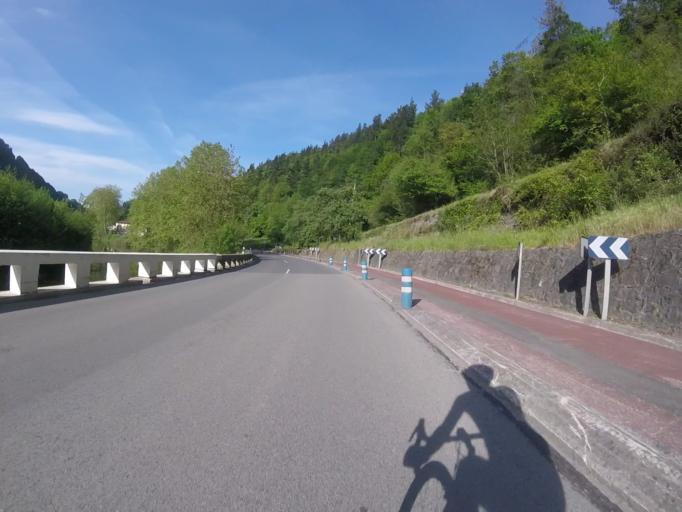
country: ES
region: Basque Country
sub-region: Provincia de Guipuzcoa
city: Legorreta
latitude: 43.0804
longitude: -2.1582
